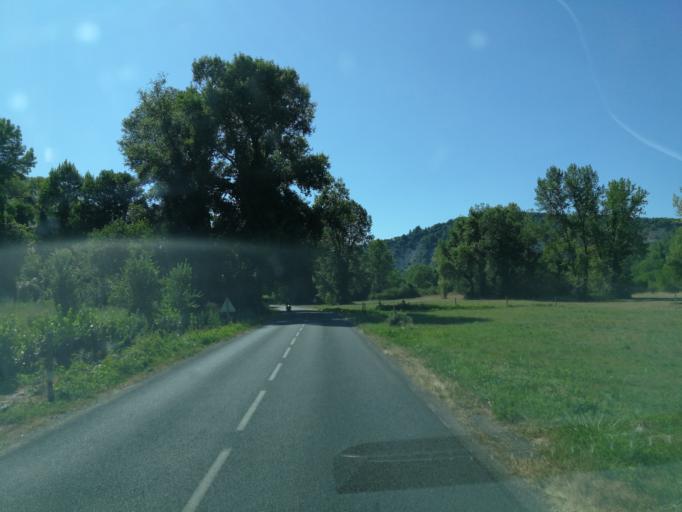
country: FR
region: Midi-Pyrenees
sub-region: Departement du Lot
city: Souillac
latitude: 44.8914
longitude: 1.4562
